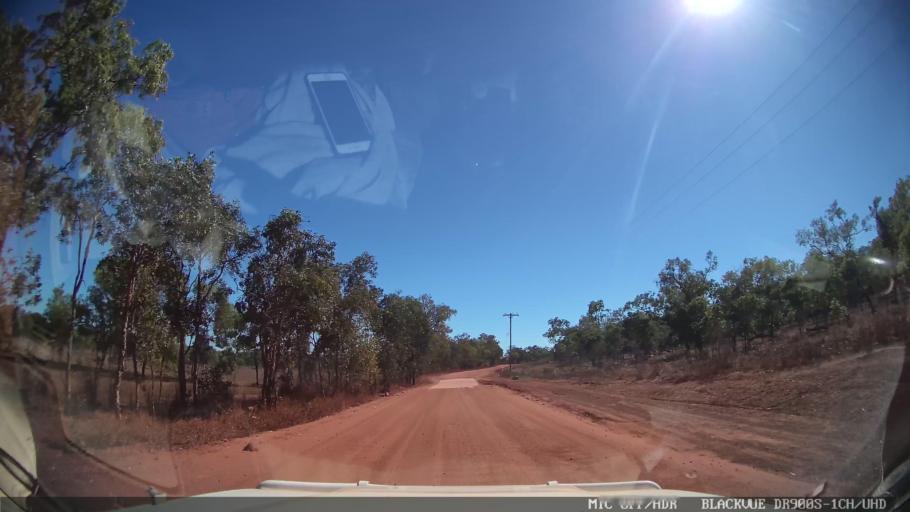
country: AU
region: Queensland
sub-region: Torres
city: Thursday Island
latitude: -10.8530
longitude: 142.3761
